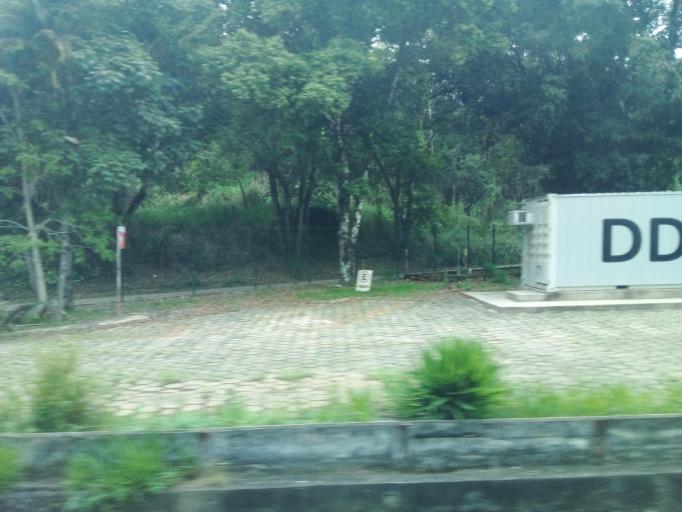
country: BR
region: Minas Gerais
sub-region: Nova Era
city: Nova Era
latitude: -19.7261
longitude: -42.9932
